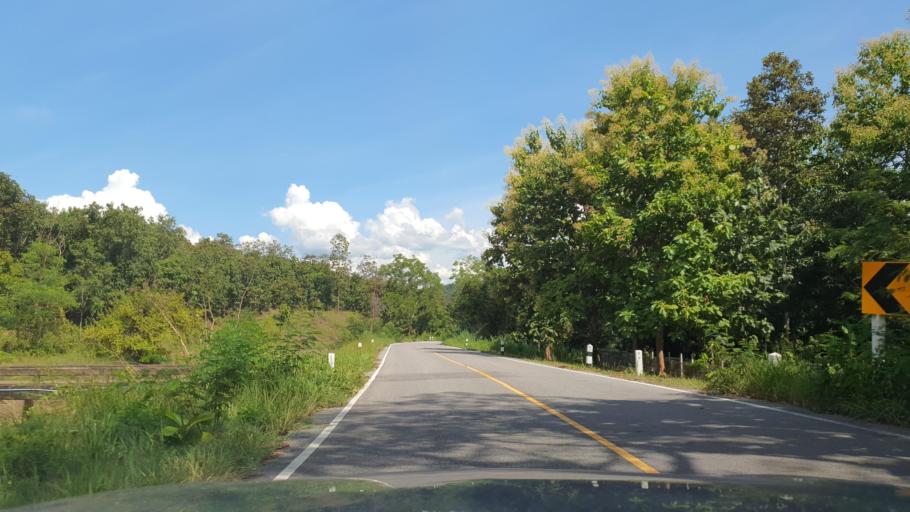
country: TH
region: Chiang Mai
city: San Kamphaeng
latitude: 18.7672
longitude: 99.1808
